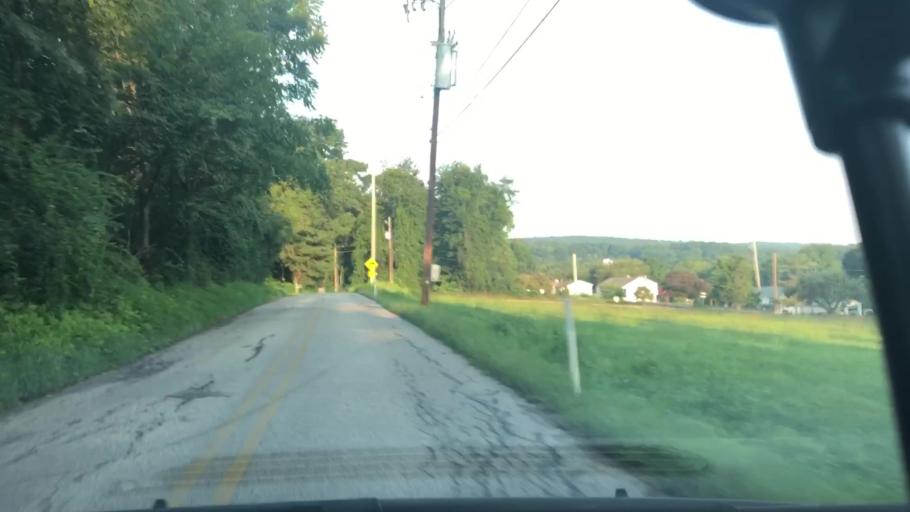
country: US
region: Pennsylvania
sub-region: Chester County
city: Kenilworth
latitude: 40.1801
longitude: -75.6493
